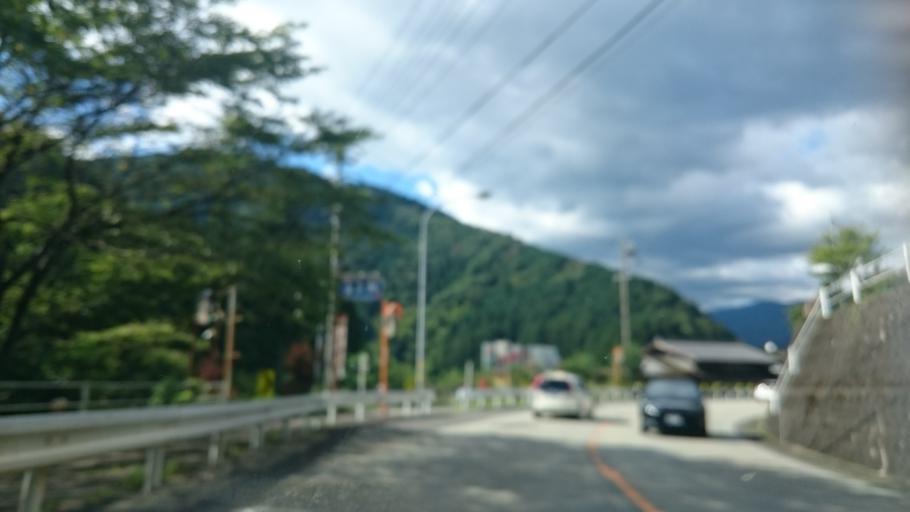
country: JP
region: Gifu
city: Gujo
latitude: 35.7761
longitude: 137.2529
